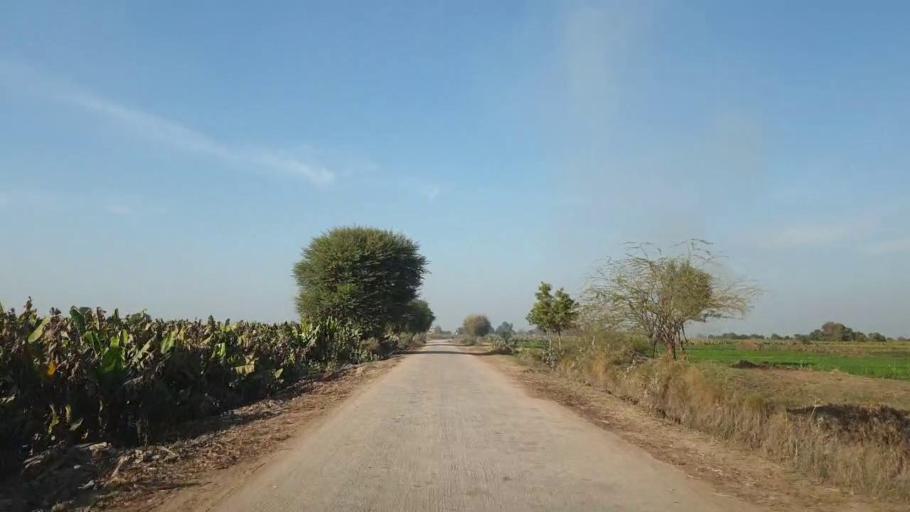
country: PK
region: Sindh
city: Tando Adam
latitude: 25.7031
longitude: 68.7023
